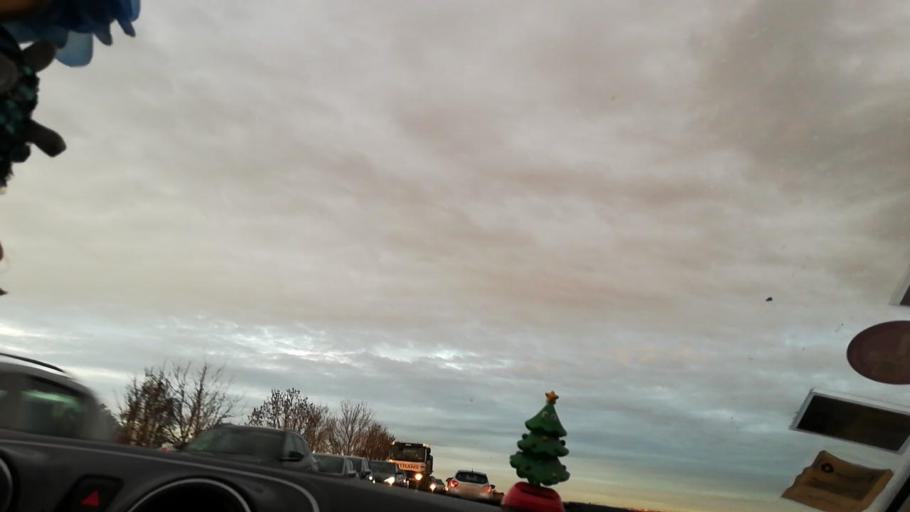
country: FR
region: Ile-de-France
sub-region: Departement de Seine-et-Marne
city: Claye-Souilly
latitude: 48.9606
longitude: 2.6644
